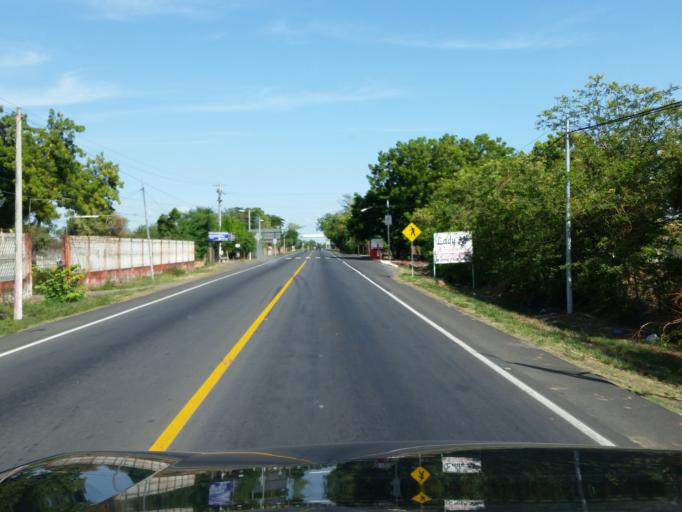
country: NI
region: Leon
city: Leon
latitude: 12.4126
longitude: -86.8647
